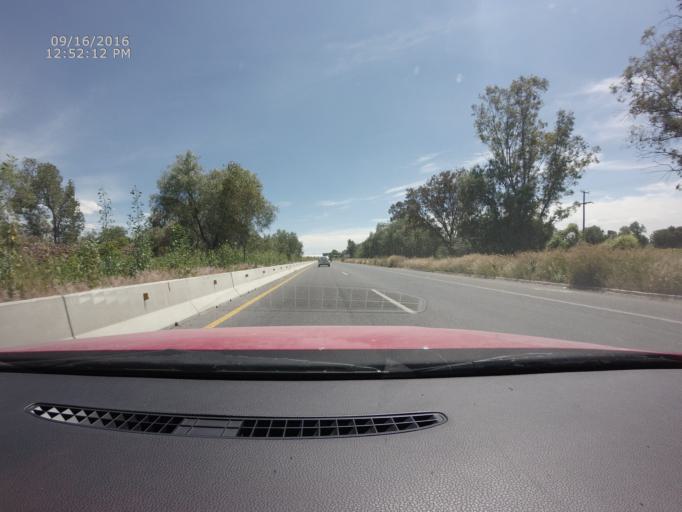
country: MX
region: Queretaro
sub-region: Colon
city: Purisima de Cubos (La Purisima)
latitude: 20.6161
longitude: -100.1457
